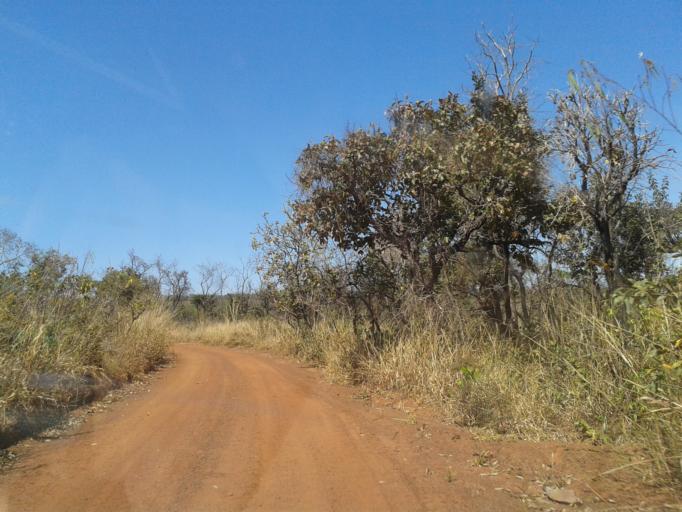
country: BR
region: Minas Gerais
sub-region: Monte Alegre De Minas
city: Monte Alegre de Minas
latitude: -18.8279
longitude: -49.1118
